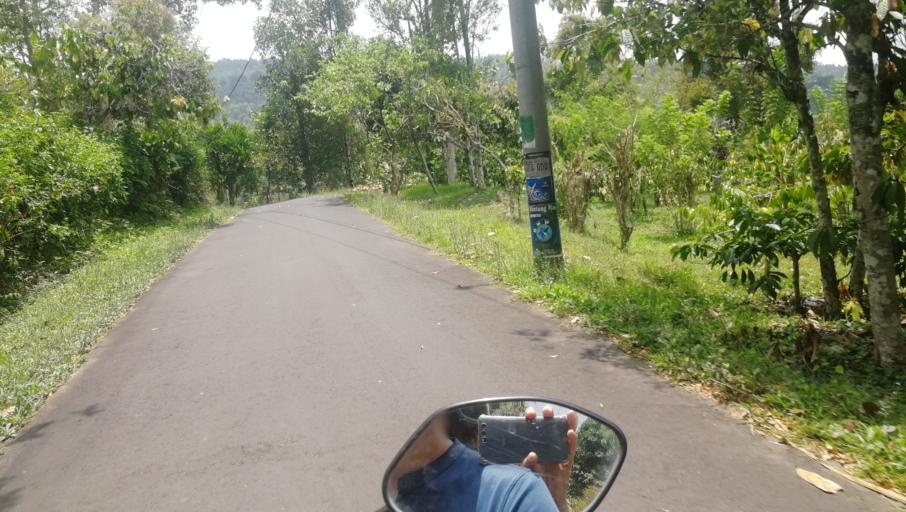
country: ID
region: Bali
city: Munduk
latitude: -8.2903
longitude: 115.0431
